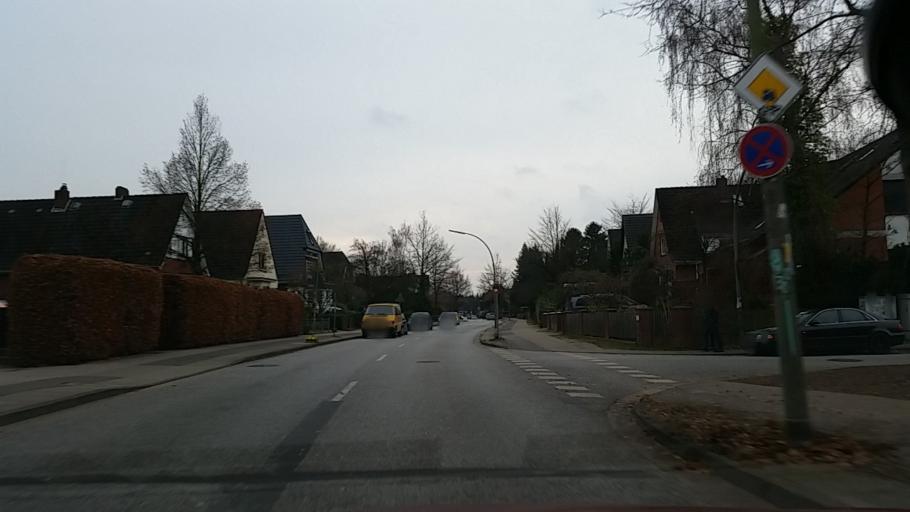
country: DE
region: Hamburg
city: Stellingen
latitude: 53.6273
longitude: 9.9508
